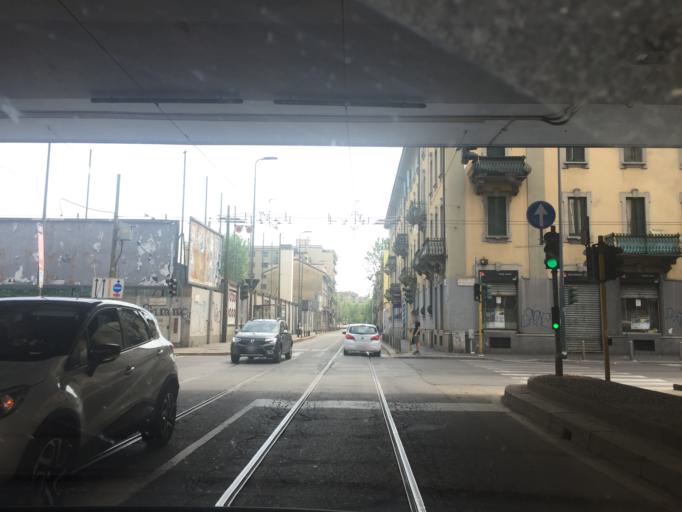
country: IT
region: Lombardy
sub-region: Citta metropolitana di Milano
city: Novate Milanese
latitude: 45.4914
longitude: 9.1532
